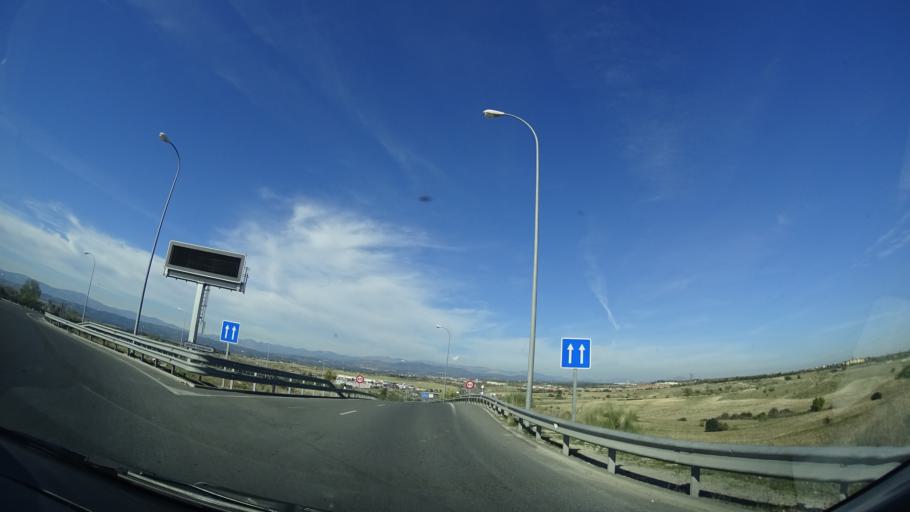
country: ES
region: Madrid
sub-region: Provincia de Madrid
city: Majadahonda
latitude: 40.4788
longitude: -3.8949
